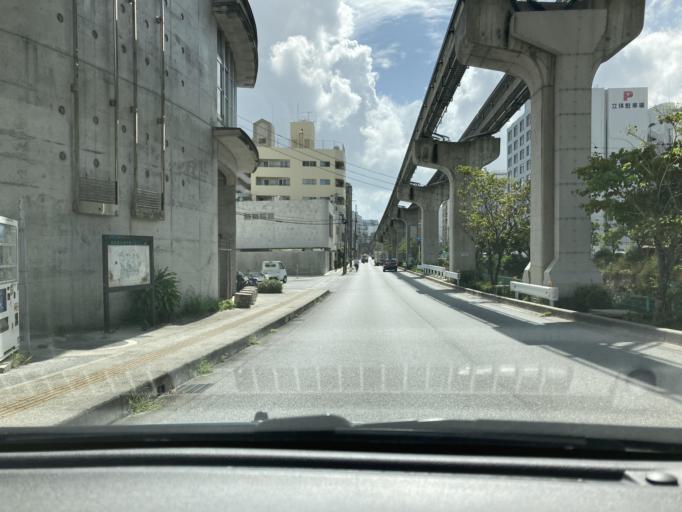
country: JP
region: Okinawa
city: Naha-shi
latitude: 26.2184
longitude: 127.6833
